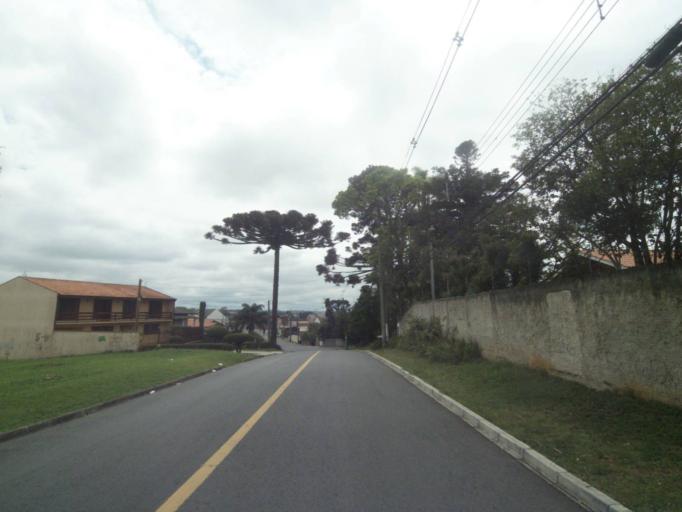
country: BR
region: Parana
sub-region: Curitiba
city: Curitiba
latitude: -25.3875
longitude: -49.2807
